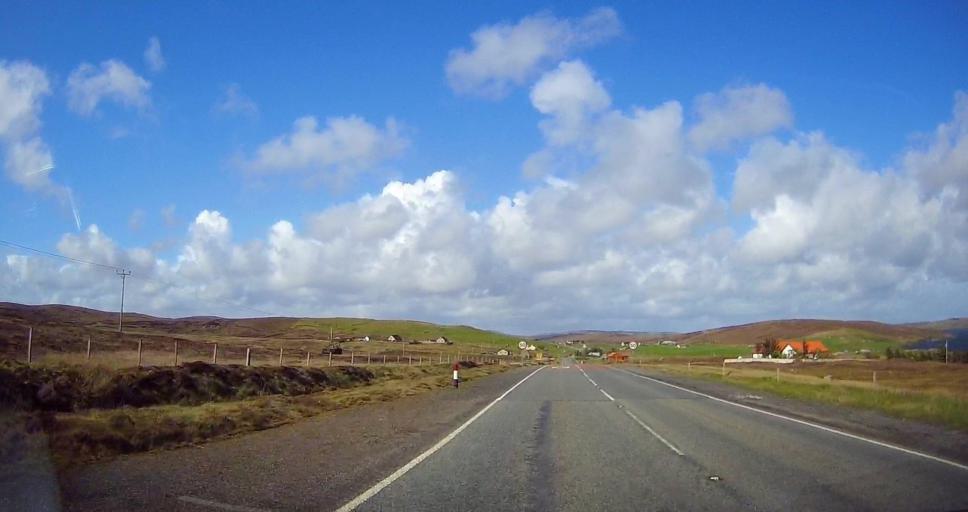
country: GB
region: Scotland
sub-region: Shetland Islands
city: Lerwick
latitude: 60.2308
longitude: -1.2367
